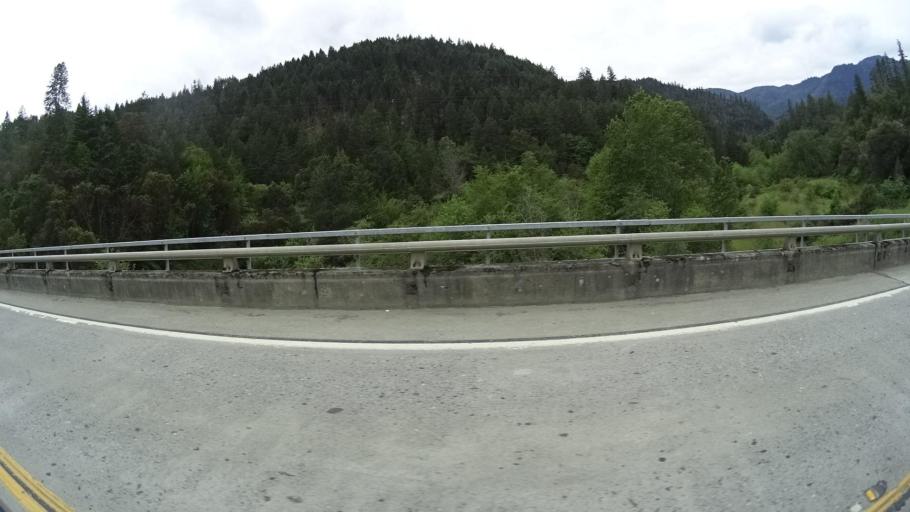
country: US
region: California
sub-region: Humboldt County
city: Willow Creek
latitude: 40.9431
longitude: -123.6330
